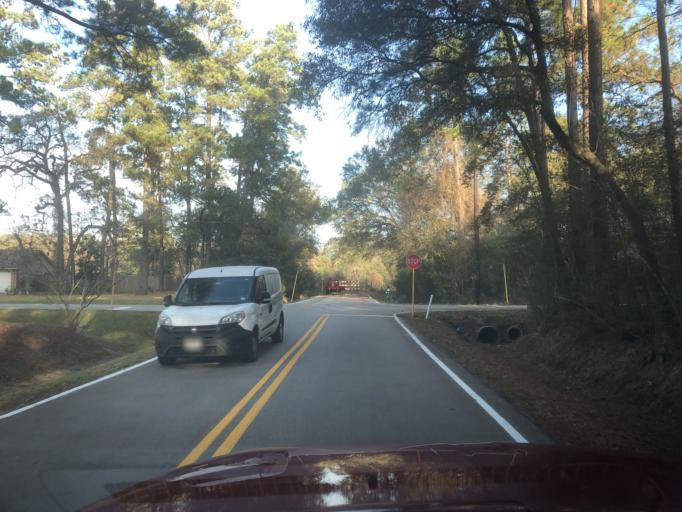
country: US
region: Texas
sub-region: Harris County
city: Spring
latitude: 30.0195
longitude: -95.4785
